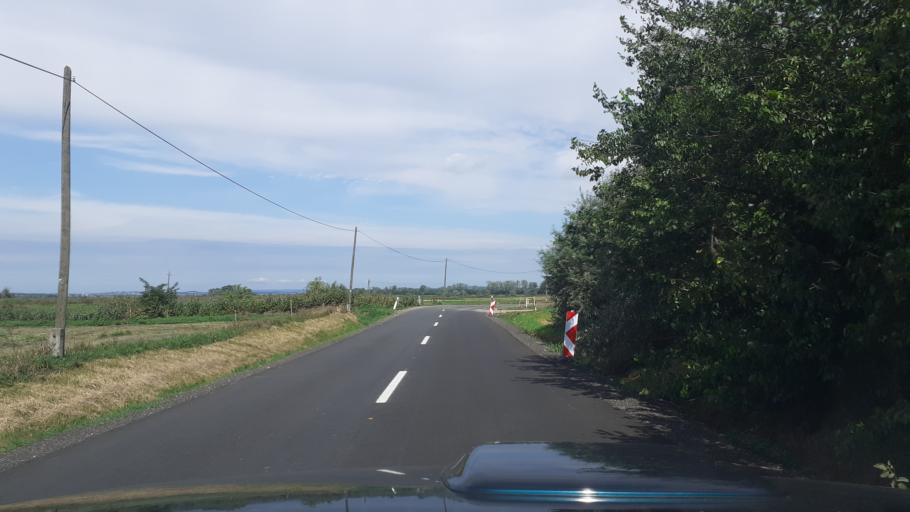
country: HU
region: Fejer
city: Seregelyes
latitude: 47.1399
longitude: 18.5756
